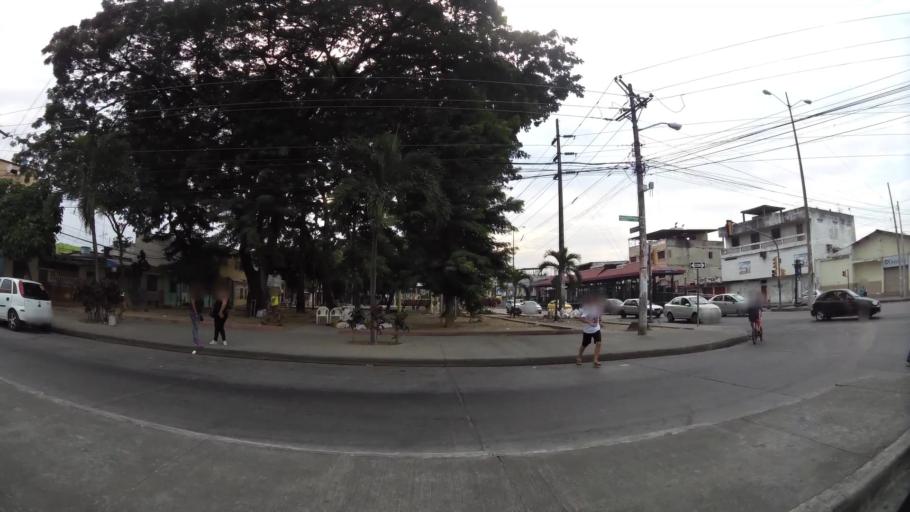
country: EC
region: Guayas
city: Guayaquil
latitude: -2.2525
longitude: -79.8818
